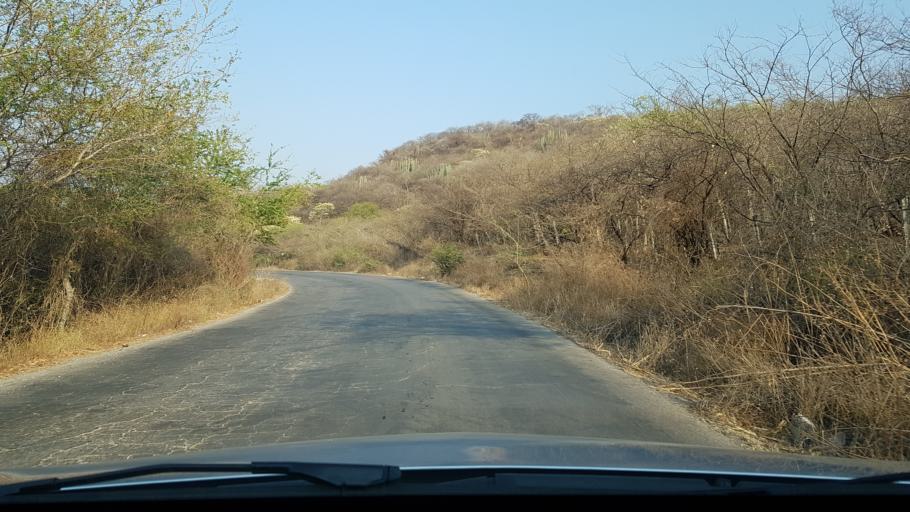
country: MX
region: Morelos
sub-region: Tepalcingo
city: Zacapalco
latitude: 18.6371
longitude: -99.0131
